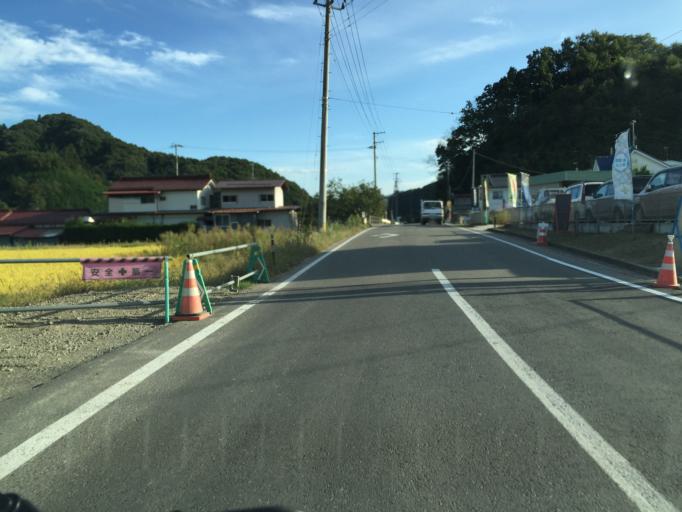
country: JP
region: Fukushima
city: Hobaramachi
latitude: 37.7297
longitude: 140.6047
